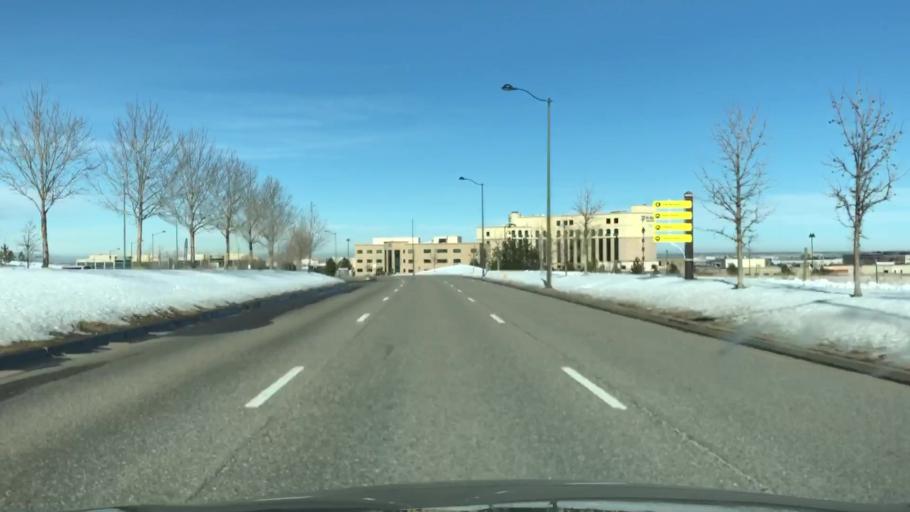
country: US
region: Colorado
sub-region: Douglas County
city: Meridian
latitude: 39.5254
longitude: -104.8722
